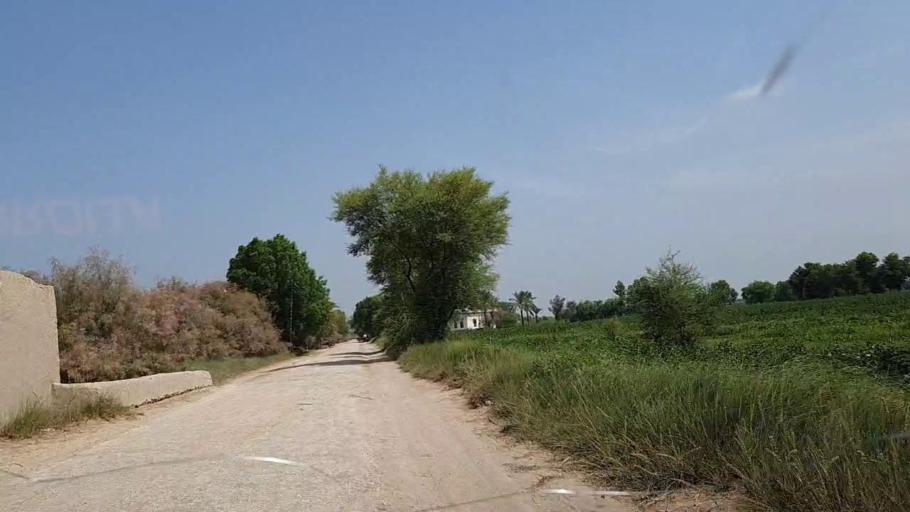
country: PK
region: Sindh
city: Adilpur
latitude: 27.8280
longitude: 69.2959
